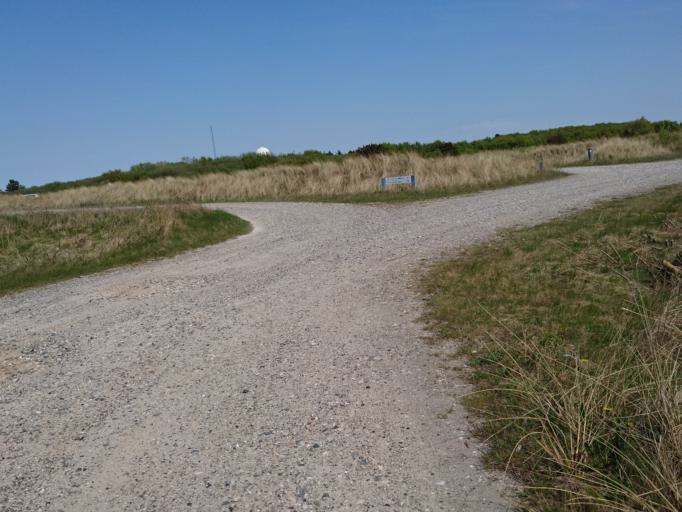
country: DK
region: North Denmark
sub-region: Frederikshavn Kommune
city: Skagen
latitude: 57.7384
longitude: 10.5957
